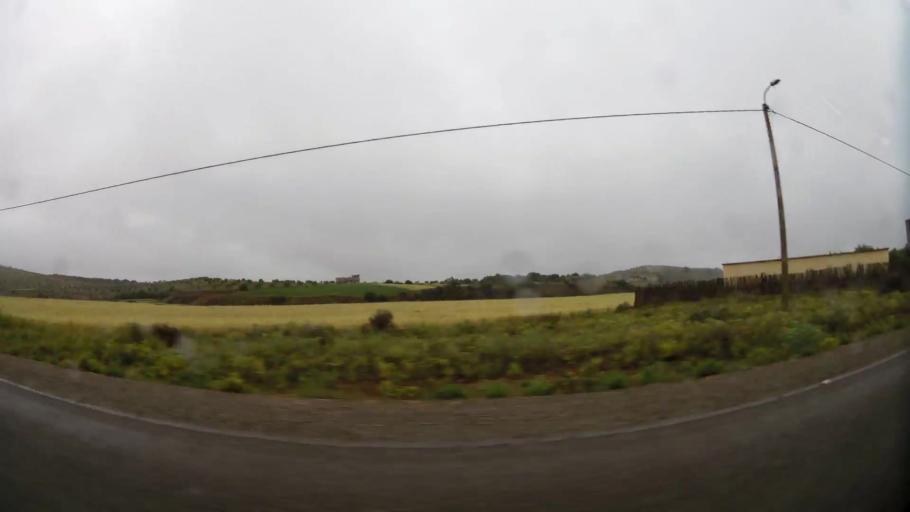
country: MA
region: Oriental
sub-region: Nador
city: Boudinar
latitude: 35.1163
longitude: -3.5767
